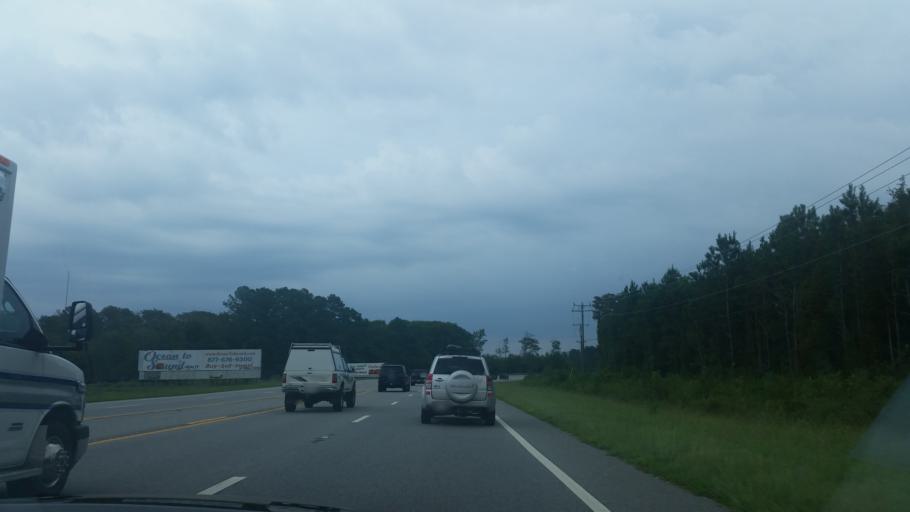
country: US
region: North Carolina
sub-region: Currituck County
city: Moyock
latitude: 36.4685
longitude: -76.1083
